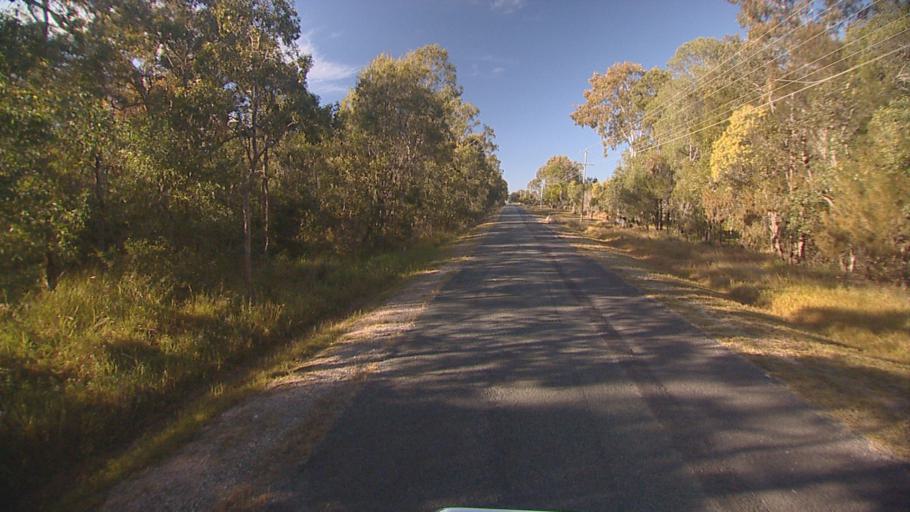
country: AU
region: Queensland
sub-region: Logan
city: Park Ridge South
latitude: -27.7204
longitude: 152.9822
